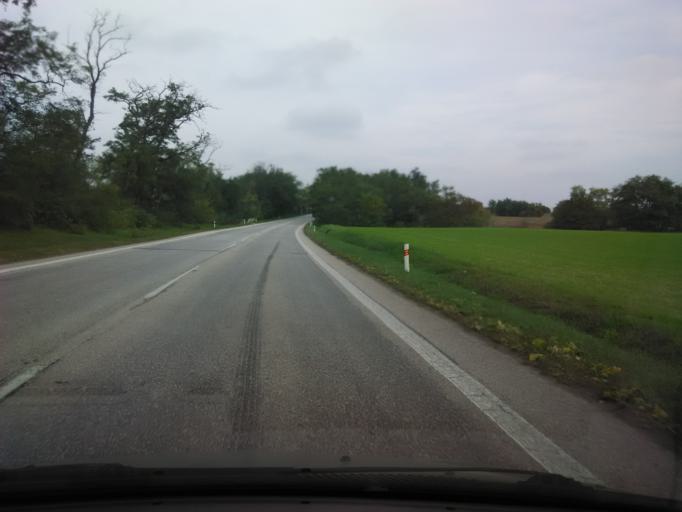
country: SK
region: Nitriansky
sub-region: Okres Komarno
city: Hurbanovo
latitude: 47.9034
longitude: 18.2062
